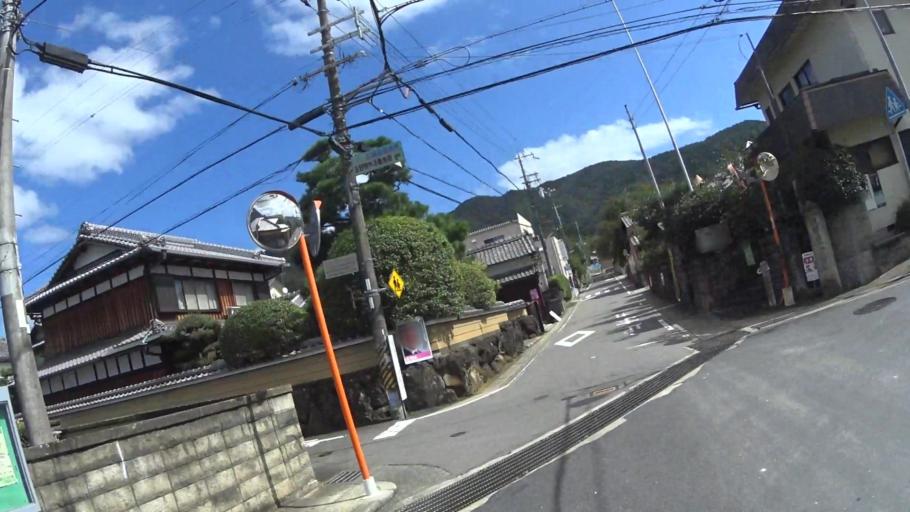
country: JP
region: Kyoto
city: Uji
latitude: 34.9359
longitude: 135.8142
